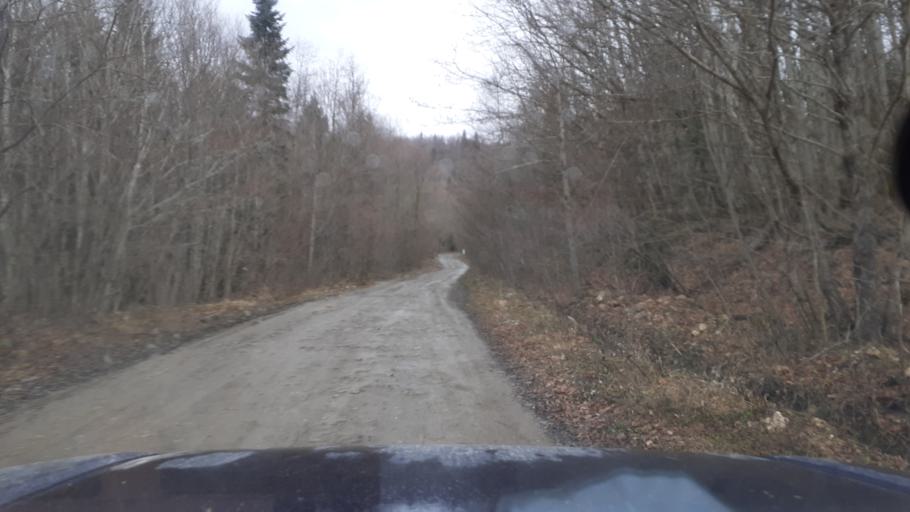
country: RU
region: Krasnodarskiy
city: Neftegorsk
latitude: 44.0658
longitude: 39.7304
